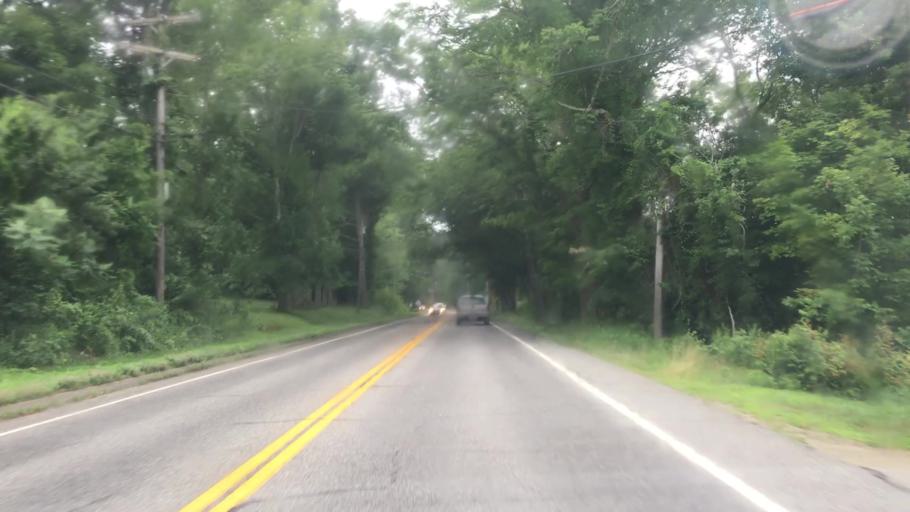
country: US
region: Maine
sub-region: Lincoln County
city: Wiscasset
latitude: 43.9925
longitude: -69.6373
